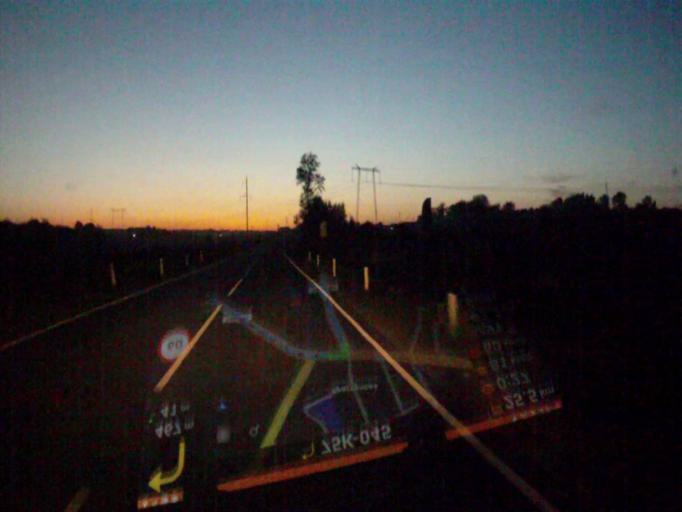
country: RU
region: Chelyabinsk
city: Chebarkul'
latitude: 55.2267
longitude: 60.4574
